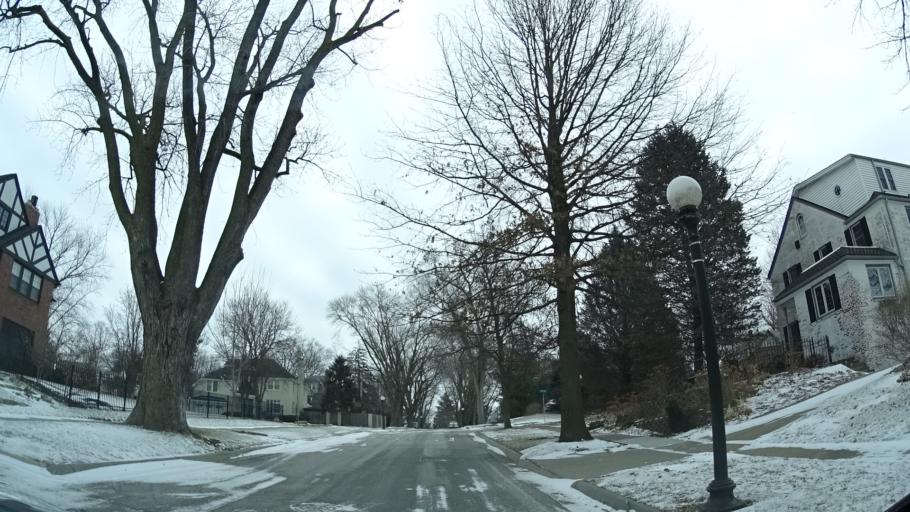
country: US
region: Nebraska
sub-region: Douglas County
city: Omaha
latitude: 41.2679
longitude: -96.0026
